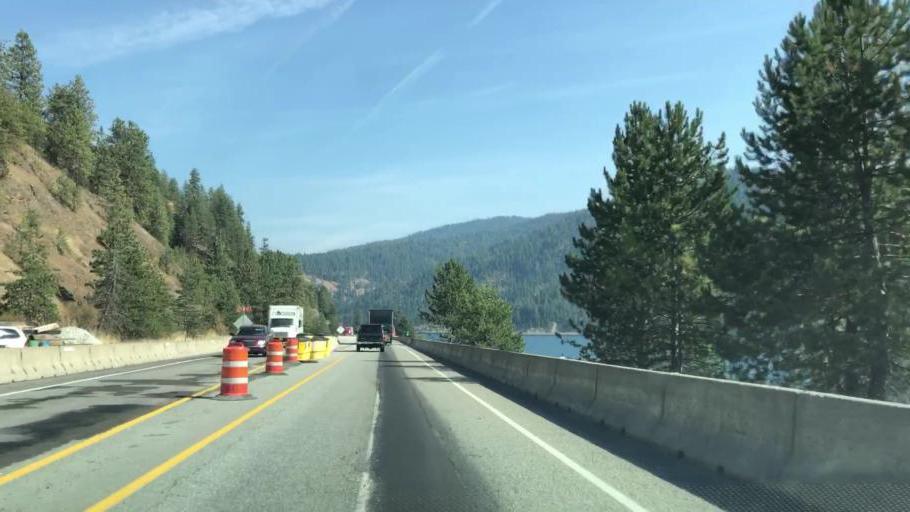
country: US
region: Idaho
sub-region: Kootenai County
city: Coeur d'Alene
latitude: 47.6265
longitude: -116.6740
